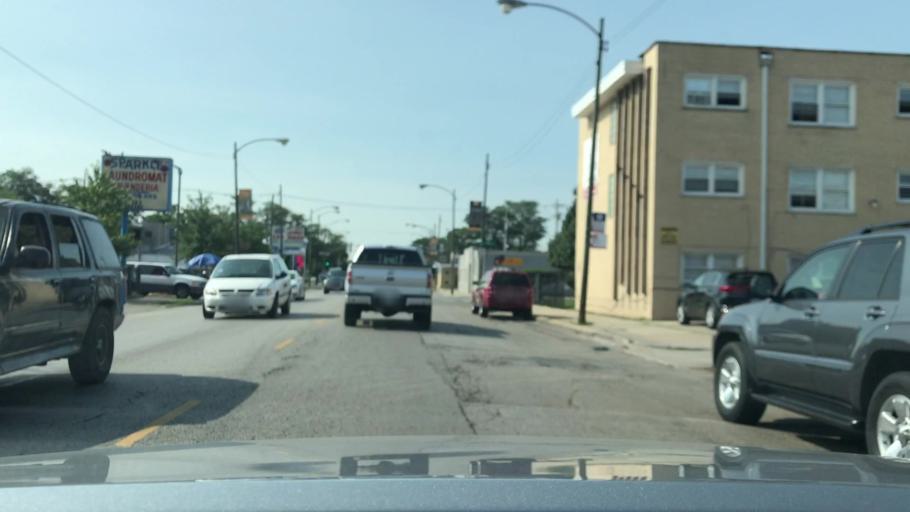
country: US
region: Illinois
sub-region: Cook County
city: Hometown
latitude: 41.7732
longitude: -87.7031
